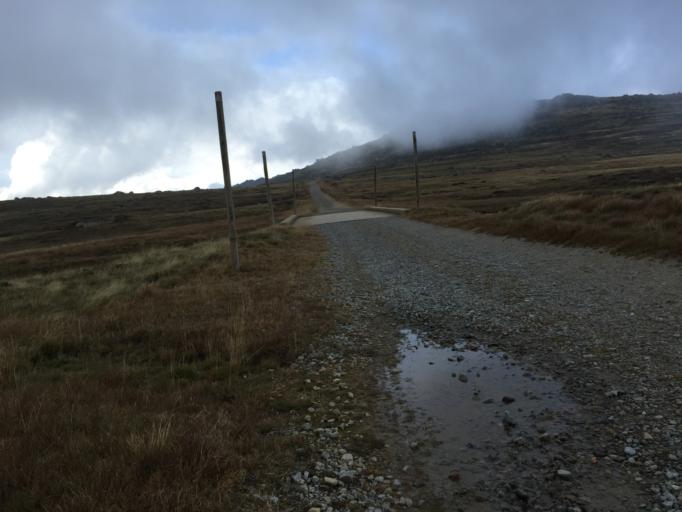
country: AU
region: New South Wales
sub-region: Snowy River
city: Jindabyne
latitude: -36.4586
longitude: 148.2965
